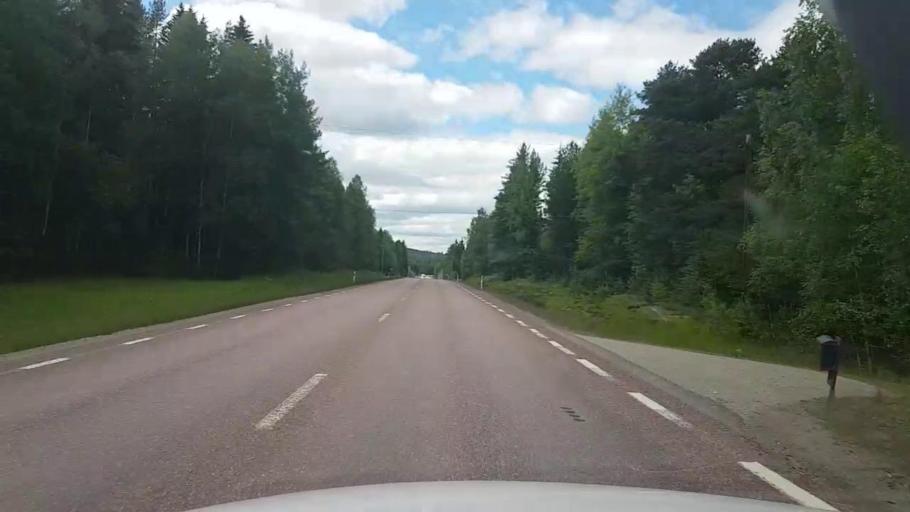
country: SE
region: Gaevleborg
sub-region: Ljusdals Kommun
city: Jaervsoe
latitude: 61.7804
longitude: 16.1419
